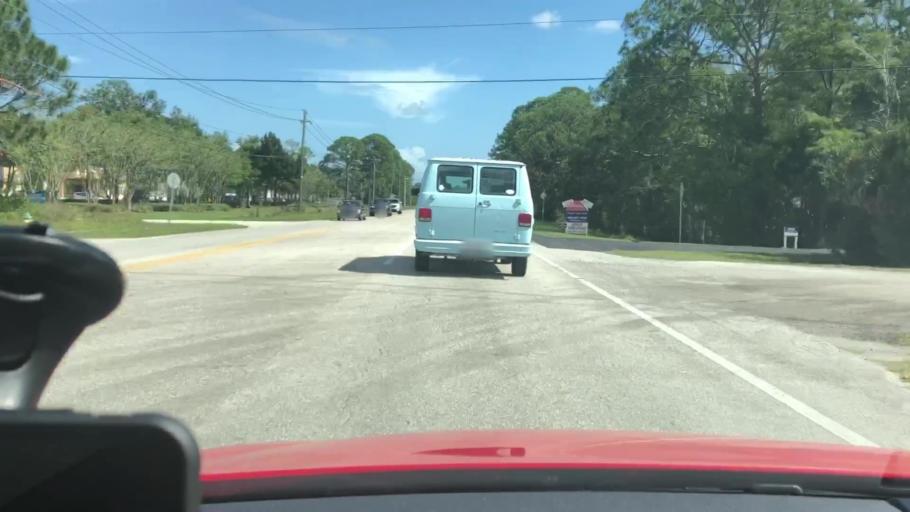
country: US
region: Florida
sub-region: Volusia County
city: Holly Hill
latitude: 29.2127
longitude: -81.0842
